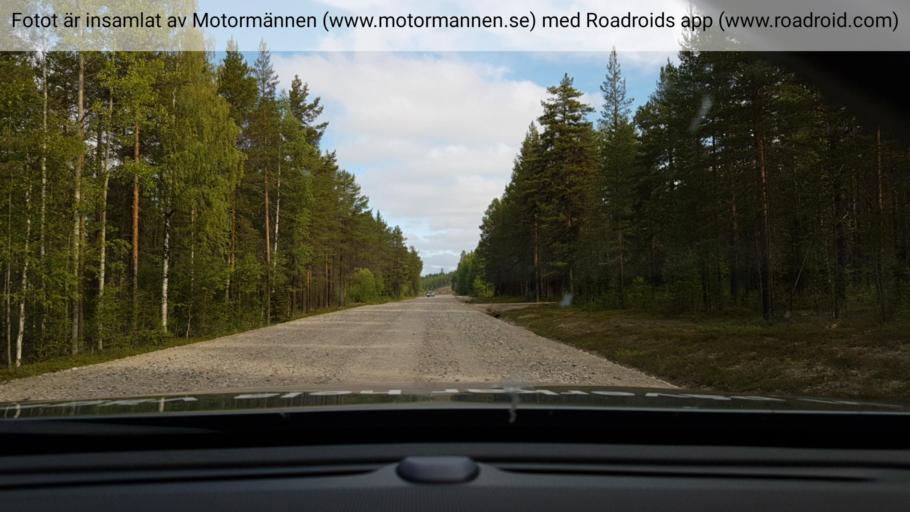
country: SE
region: Vaesterbotten
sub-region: Norsjo Kommun
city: Norsjoe
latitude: 64.6157
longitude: 19.2898
